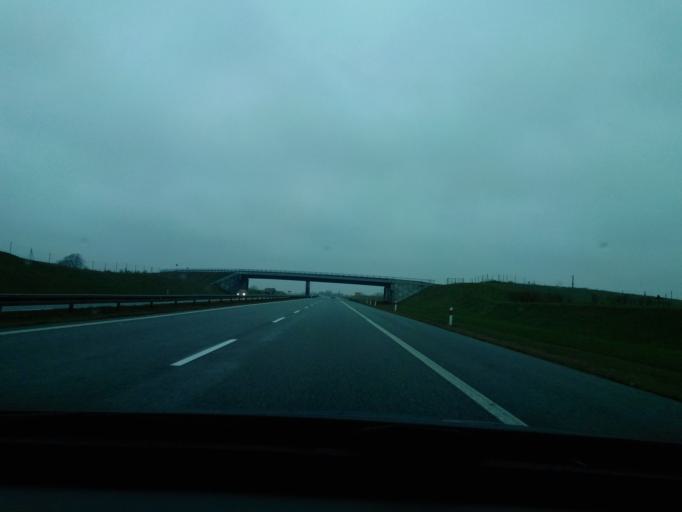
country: PL
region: Pomeranian Voivodeship
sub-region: Powiat gdanski
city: Pszczolki
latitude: 54.1687
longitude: 18.6542
